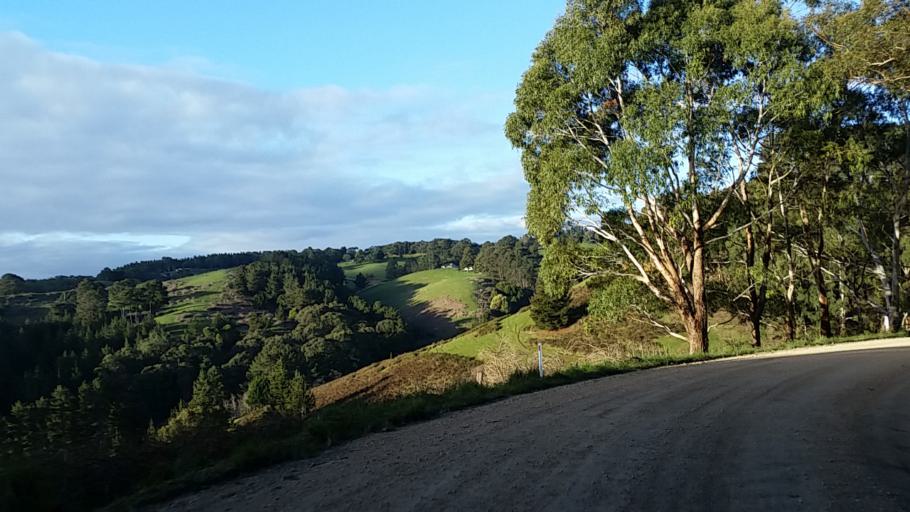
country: AU
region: South Australia
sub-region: Adelaide Hills
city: Lobethal
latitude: -34.8998
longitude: 138.8127
